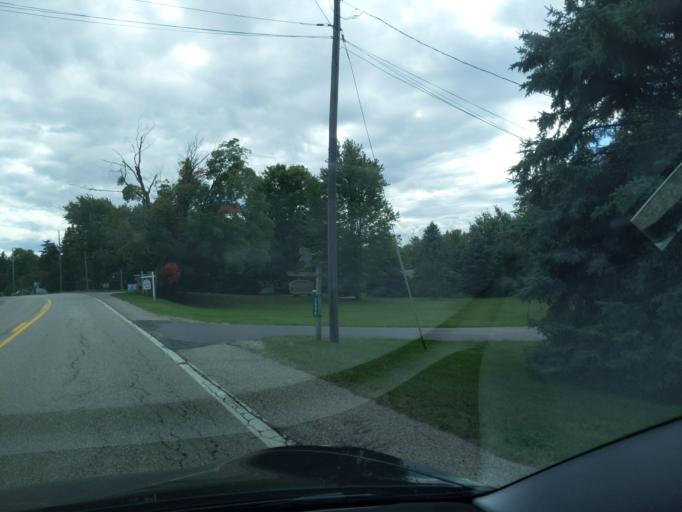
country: US
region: Michigan
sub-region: Kalkaska County
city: Rapid City
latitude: 44.9182
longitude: -85.2856
